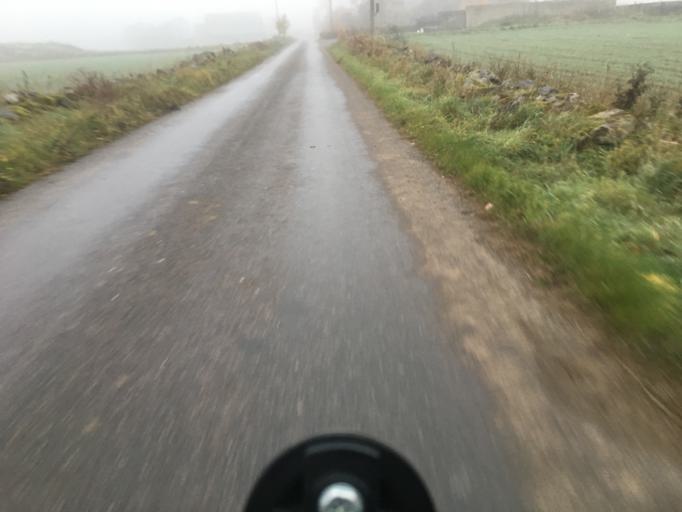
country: SE
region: Blekinge
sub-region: Karlshamns Kommun
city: Morrum
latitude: 56.1797
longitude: 14.7810
